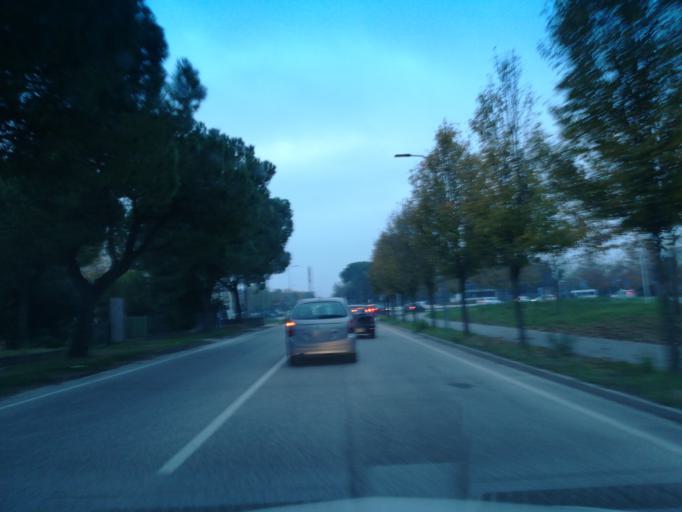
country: IT
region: Emilia-Romagna
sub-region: Provincia di Ravenna
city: Faenza
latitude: 44.2966
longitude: 11.8887
